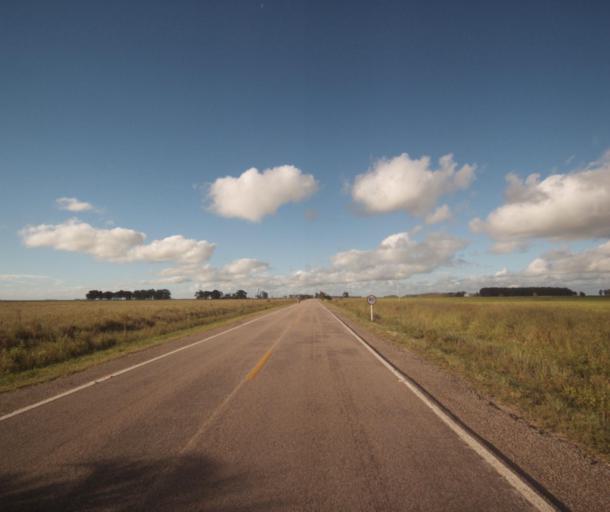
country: BR
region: Rio Grande do Sul
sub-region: Arroio Grande
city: Arroio Grande
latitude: -32.4513
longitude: -52.5706
